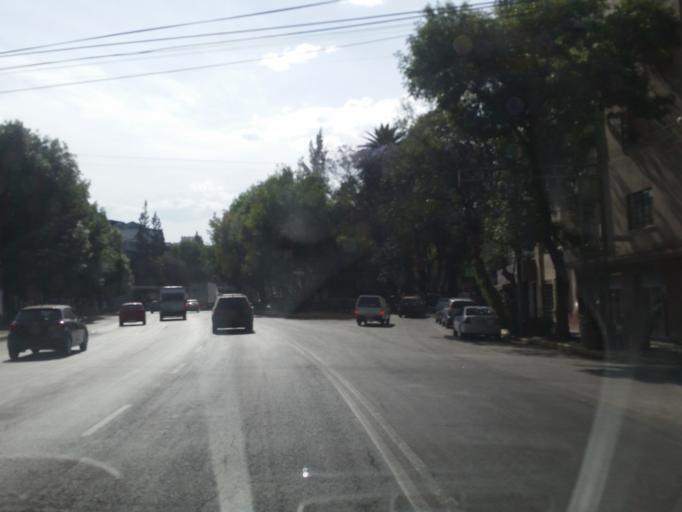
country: MX
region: Mexico City
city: Benito Juarez
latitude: 19.4058
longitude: -99.1758
